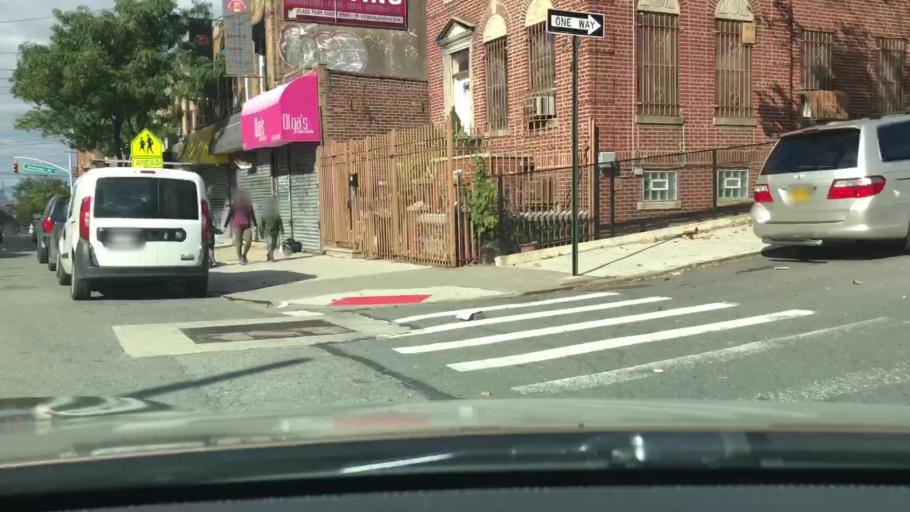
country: US
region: New York
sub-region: Queens County
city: Long Island City
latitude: 40.7131
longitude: -73.9080
